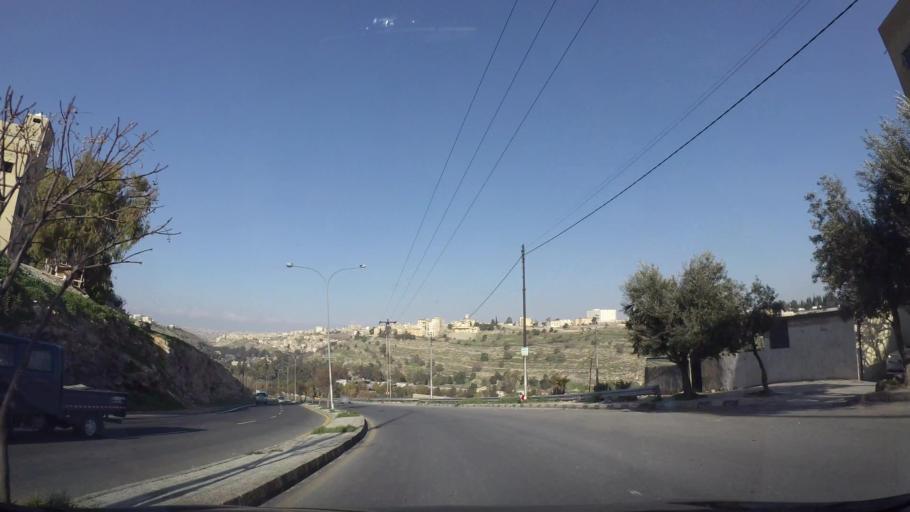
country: JO
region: Amman
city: Amman
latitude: 31.9740
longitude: 35.9683
